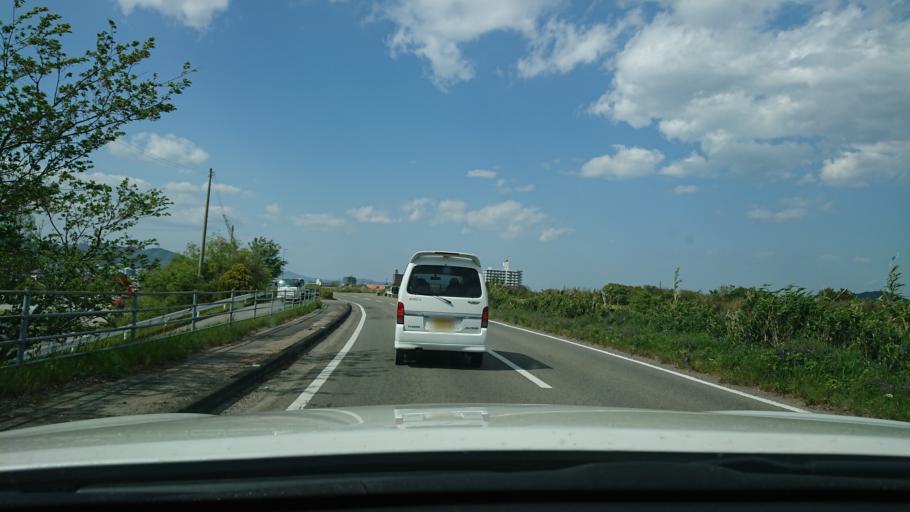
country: JP
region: Tokushima
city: Komatsushimacho
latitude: 34.0103
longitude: 134.5550
